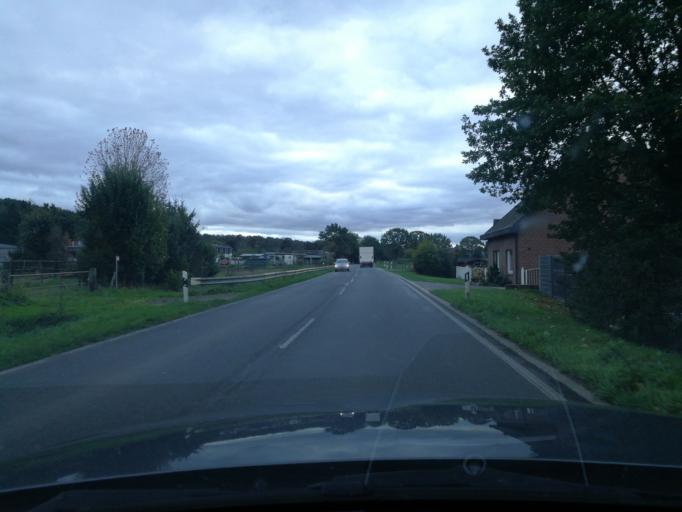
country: DE
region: North Rhine-Westphalia
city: Straelen
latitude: 51.4299
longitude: 6.2424
